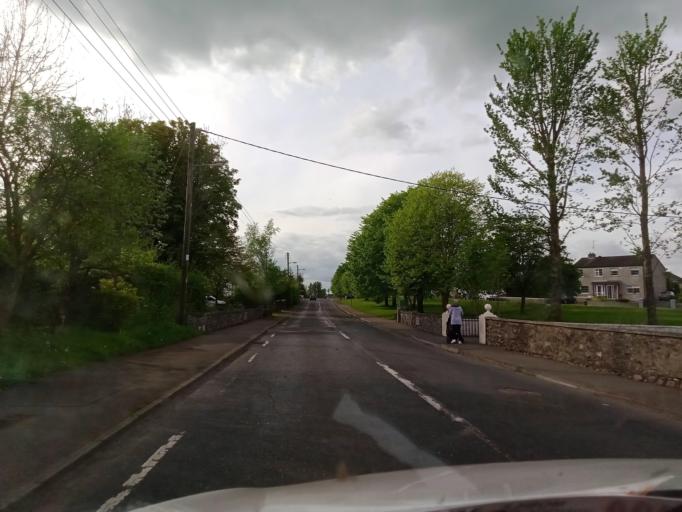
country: IE
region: Leinster
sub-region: Laois
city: Abbeyleix
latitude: 52.9164
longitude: -7.3539
